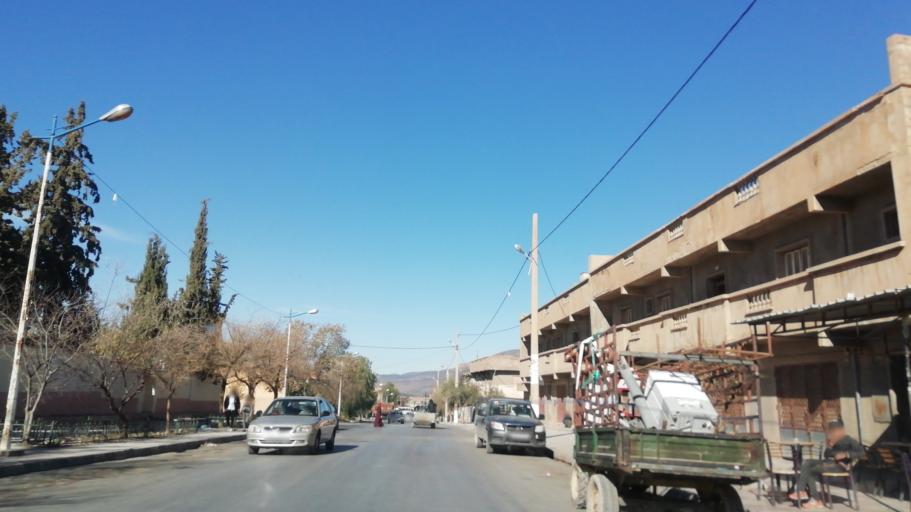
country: DZ
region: Tlemcen
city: Sebdou
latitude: 34.6495
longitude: -1.3245
